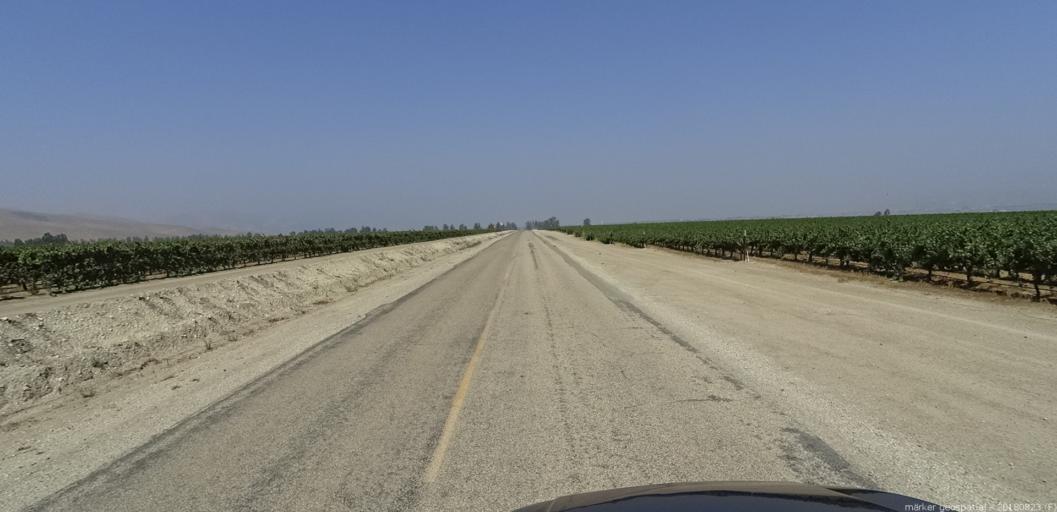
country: US
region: California
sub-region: Monterey County
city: Greenfield
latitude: 36.2686
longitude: -121.2166
